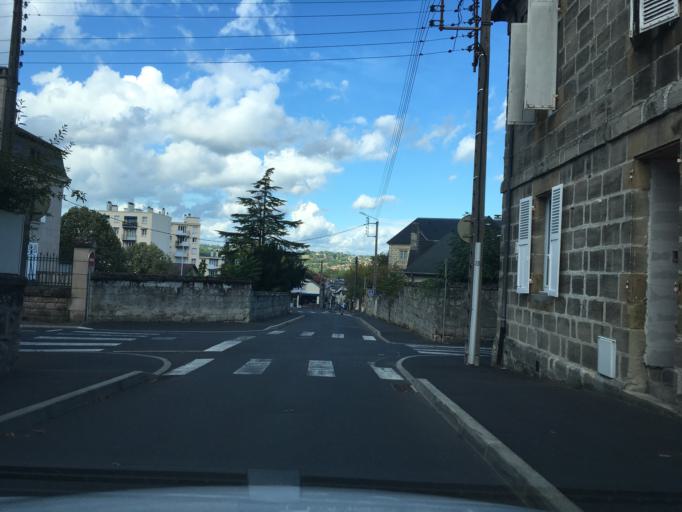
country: FR
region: Limousin
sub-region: Departement de la Correze
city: Brive-la-Gaillarde
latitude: 45.1537
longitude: 1.5280
